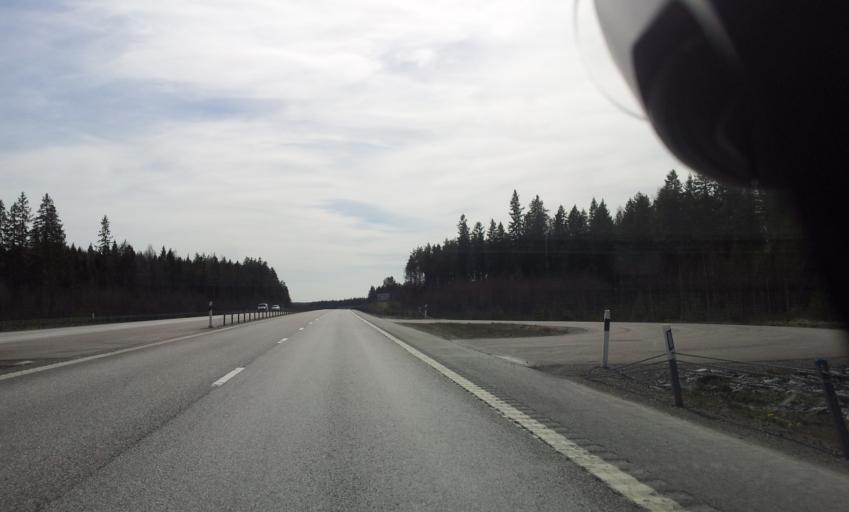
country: SE
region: Uppsala
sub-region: Tierps Kommun
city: Tierp
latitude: 60.2265
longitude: 17.4994
